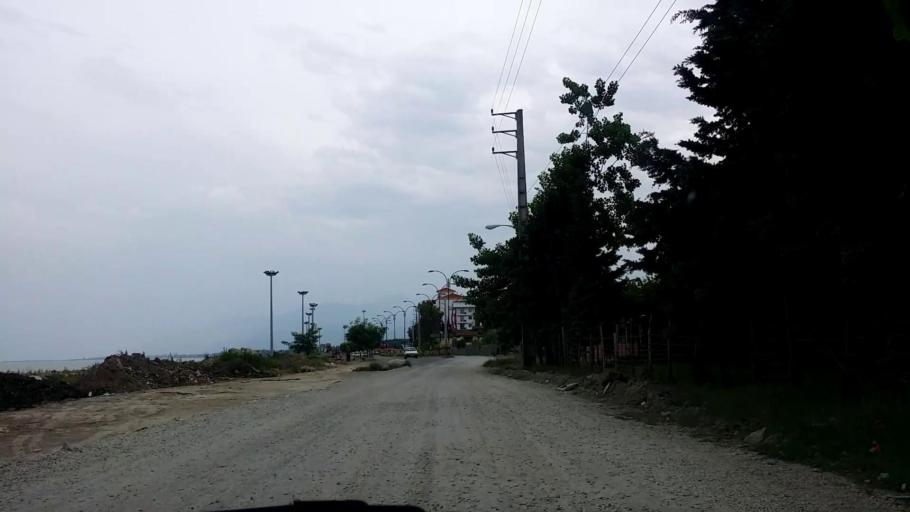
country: IR
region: Mazandaran
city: Chalus
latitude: 36.6828
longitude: 51.4340
